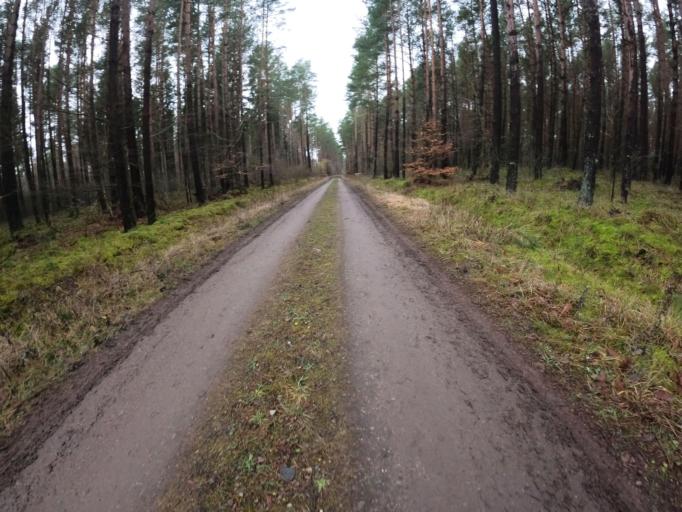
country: PL
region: West Pomeranian Voivodeship
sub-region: Powiat slawienski
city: Darlowo
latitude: 54.4197
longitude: 16.4812
